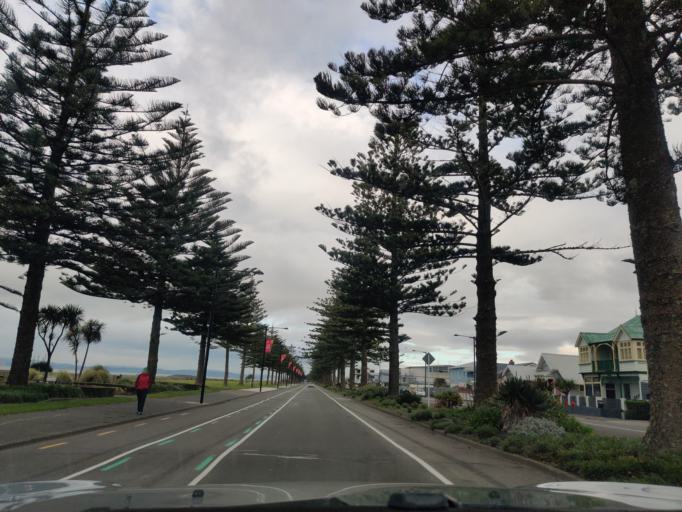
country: NZ
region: Hawke's Bay
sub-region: Napier City
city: Napier
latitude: -39.5034
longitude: 176.9183
